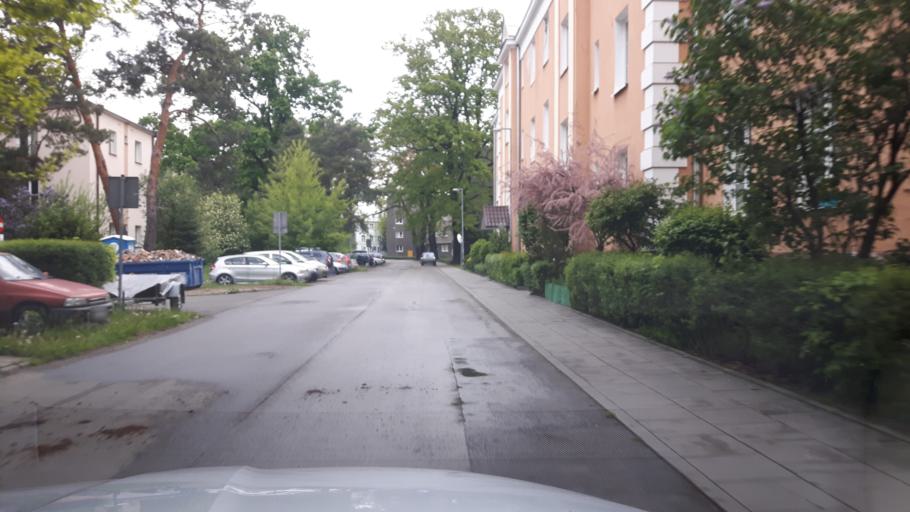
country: PL
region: Masovian Voivodeship
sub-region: Warszawa
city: Rembertow
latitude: 52.2668
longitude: 21.1797
